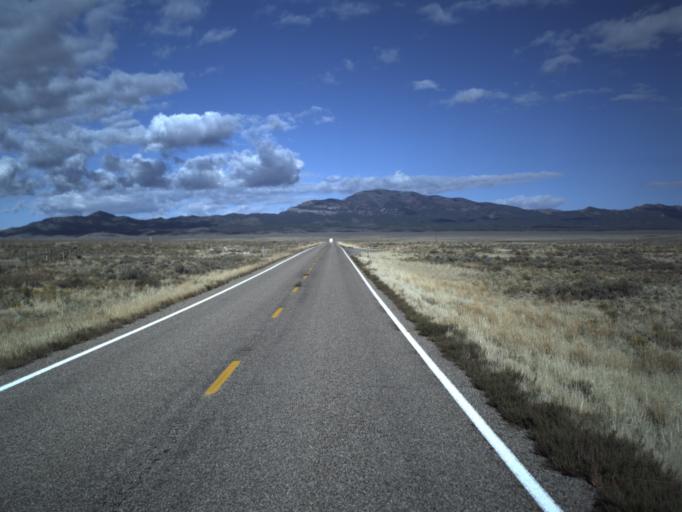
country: US
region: Utah
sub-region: Beaver County
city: Milford
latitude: 38.4268
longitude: -113.1195
